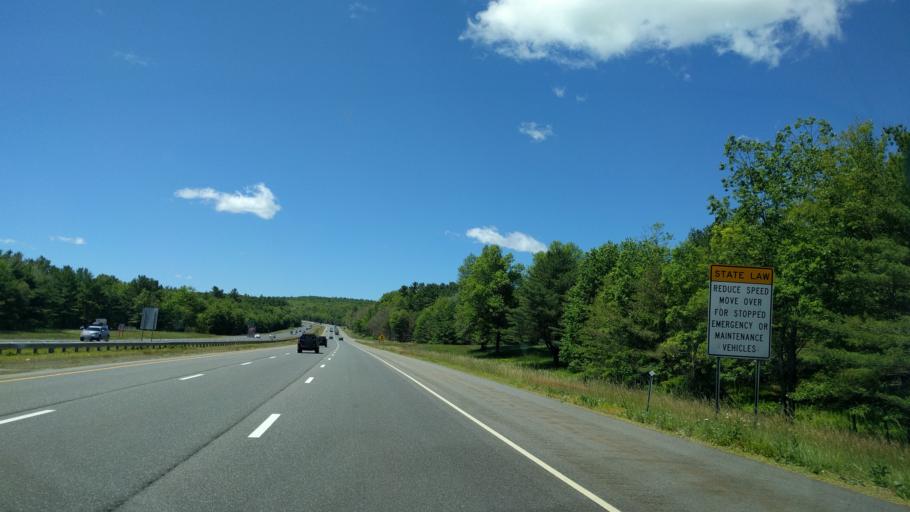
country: US
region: Massachusetts
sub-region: Hampden County
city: Holland
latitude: 42.0246
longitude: -72.1441
